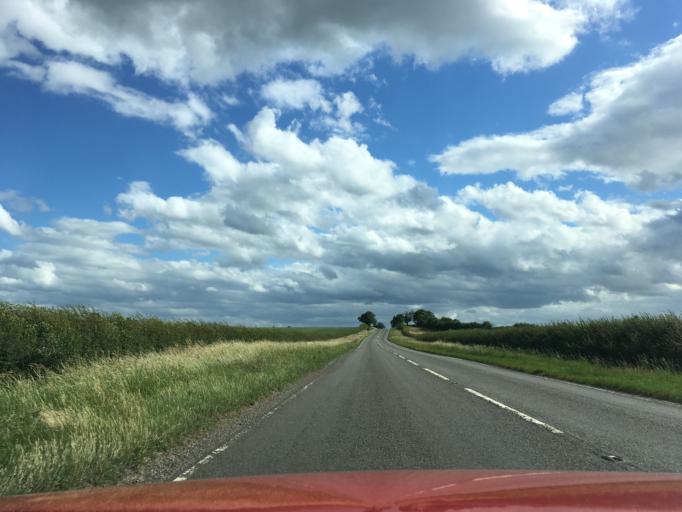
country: GB
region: England
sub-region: Warwickshire
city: Hartshill
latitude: 52.5920
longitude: -1.4781
